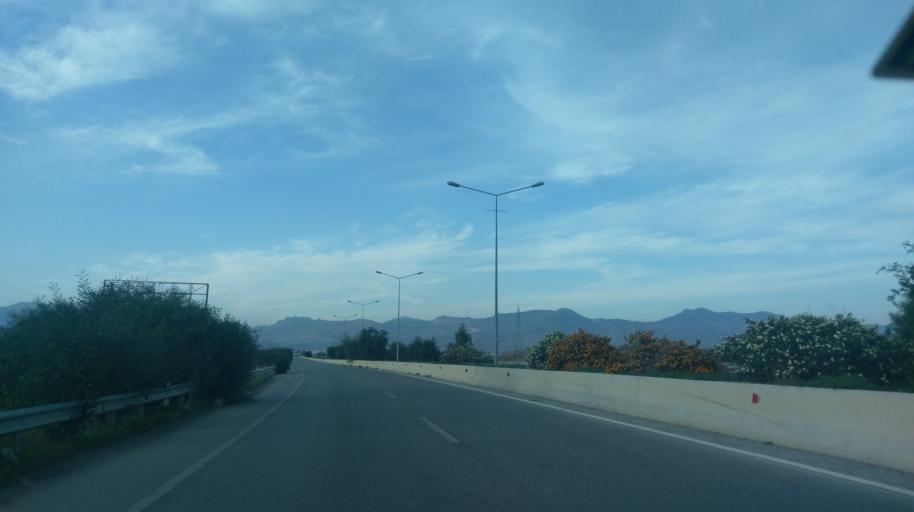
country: CY
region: Lefkosia
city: Geri
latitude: 35.1896
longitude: 33.5026
